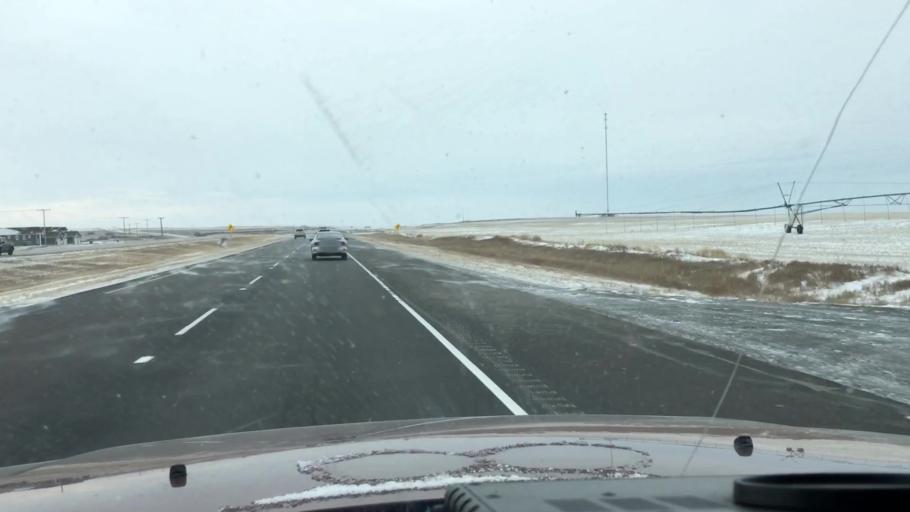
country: CA
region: Saskatchewan
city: Saskatoon
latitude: 51.7435
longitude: -106.4763
